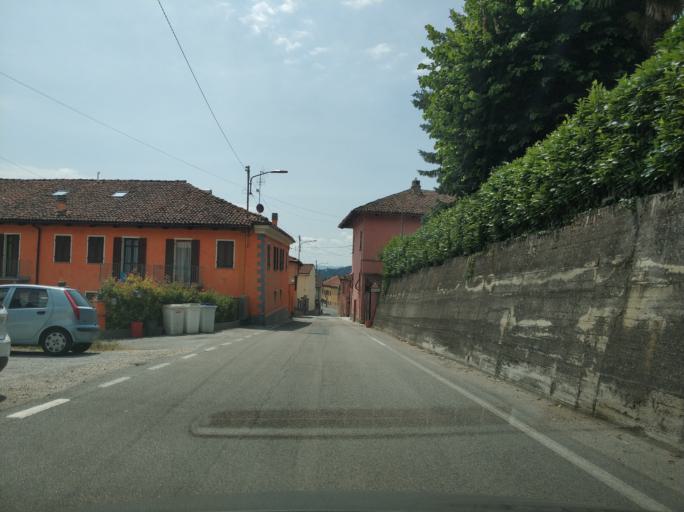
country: IT
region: Piedmont
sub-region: Provincia di Cuneo
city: Santo Stefano Roero
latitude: 44.7881
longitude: 7.9419
